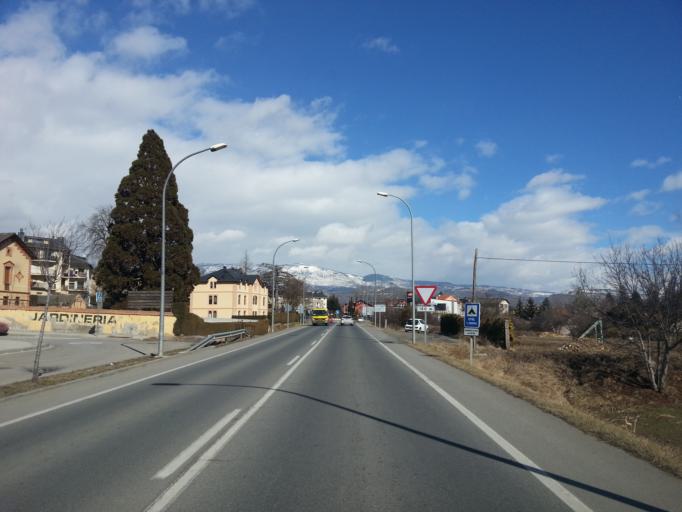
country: ES
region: Catalonia
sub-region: Provincia de Girona
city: Puigcerda
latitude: 42.4312
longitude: 1.9347
